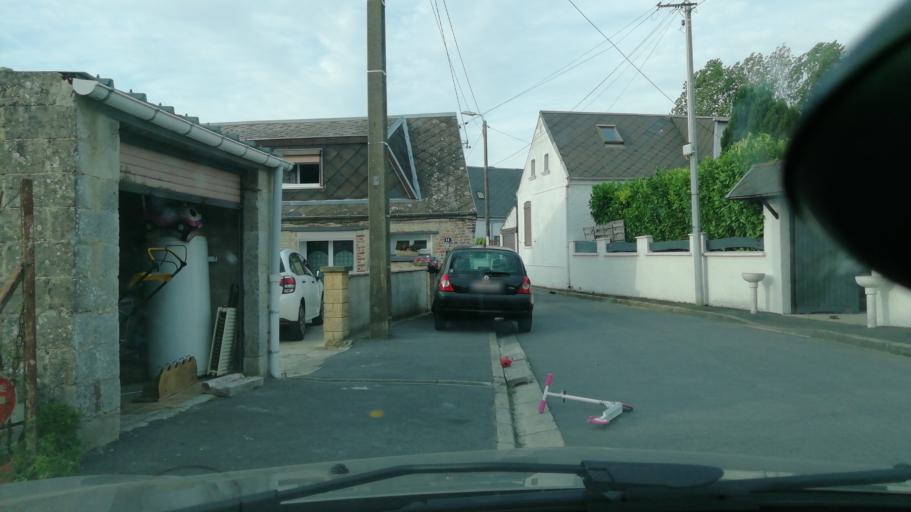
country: FR
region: Nord-Pas-de-Calais
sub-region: Departement du Nord
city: Bertry
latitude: 50.1109
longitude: 3.4735
